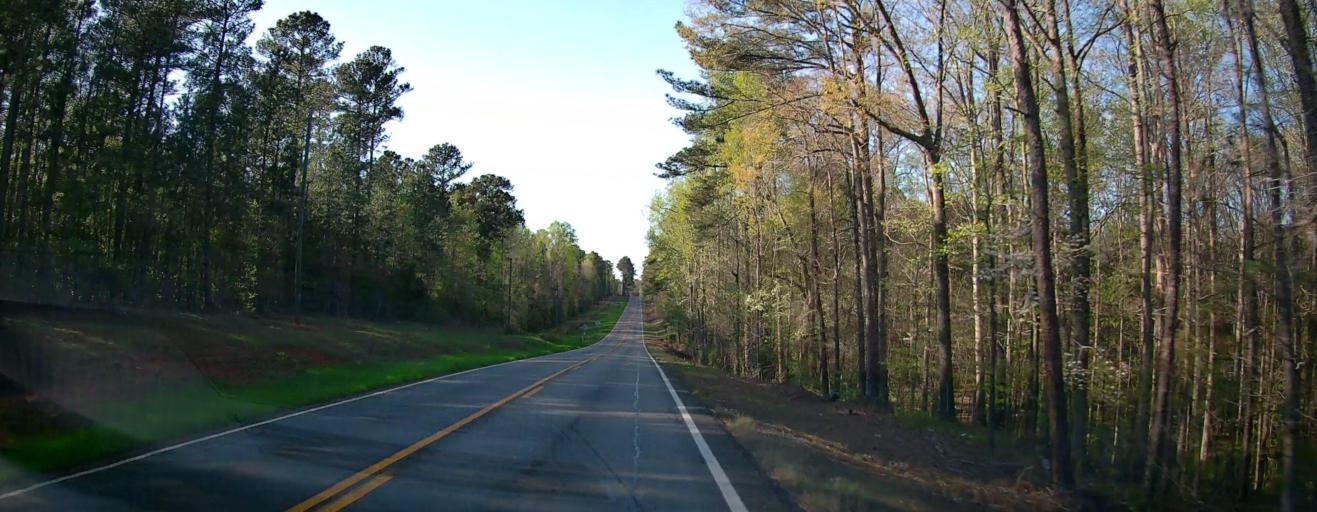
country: US
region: Georgia
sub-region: Monroe County
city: Forsyth
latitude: 33.1371
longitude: -83.9443
